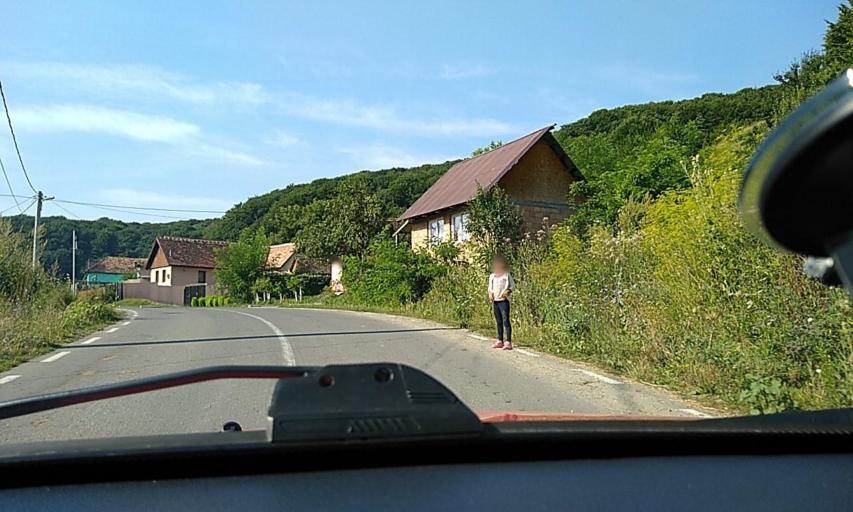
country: RO
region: Brasov
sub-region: Comuna Bunesti
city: Bunesti
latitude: 46.1015
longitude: 25.0583
